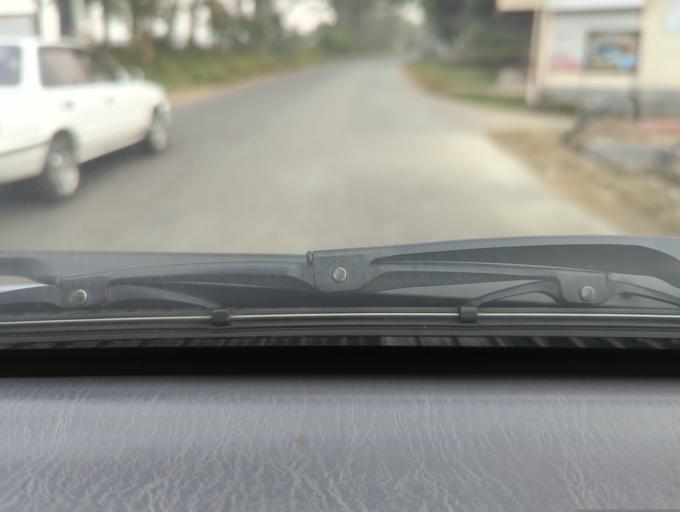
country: BD
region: Sylhet
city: Maulavi Bazar
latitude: 24.5071
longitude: 91.7324
